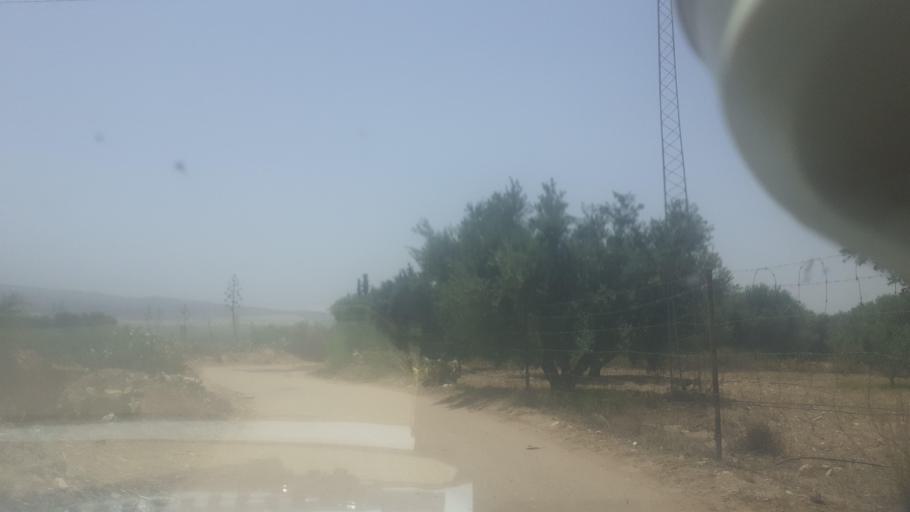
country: TN
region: Al Qasrayn
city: Kasserine
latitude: 35.2175
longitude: 8.8805
